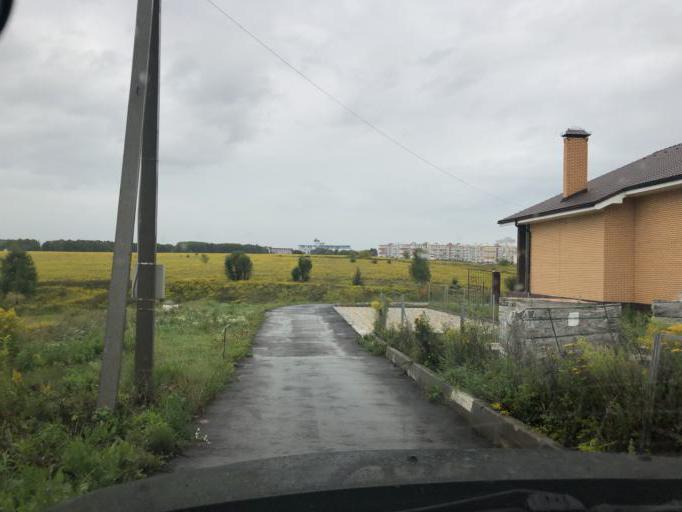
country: RU
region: Tula
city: Barsuki
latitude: 54.1986
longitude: 37.5159
